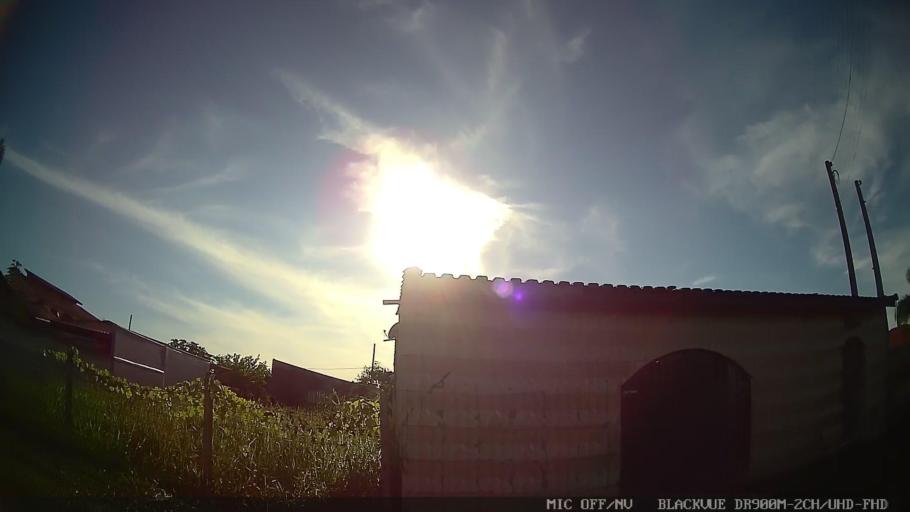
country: BR
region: Sao Paulo
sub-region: Iguape
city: Iguape
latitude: -24.7588
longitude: -47.5714
